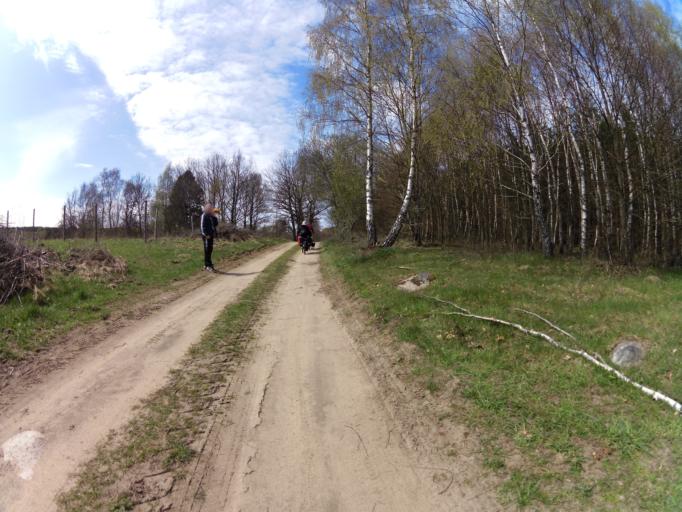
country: PL
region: West Pomeranian Voivodeship
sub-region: Powiat szczecinecki
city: Szczecinek
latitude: 53.7787
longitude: 16.6219
